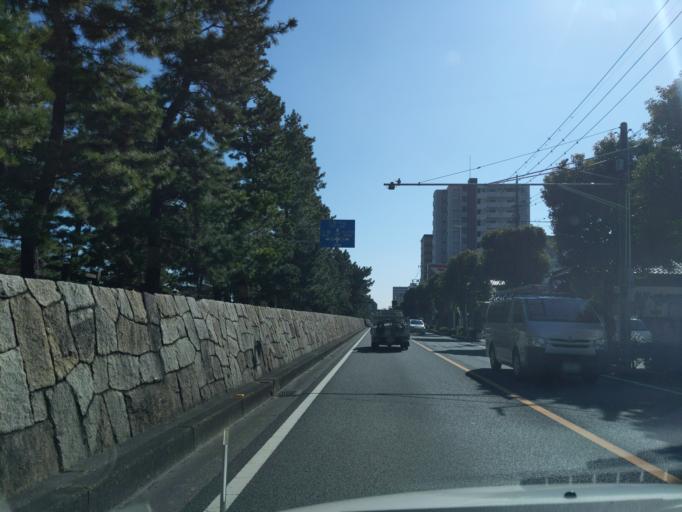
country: JP
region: Saitama
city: Soka
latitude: 35.8407
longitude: 139.8052
